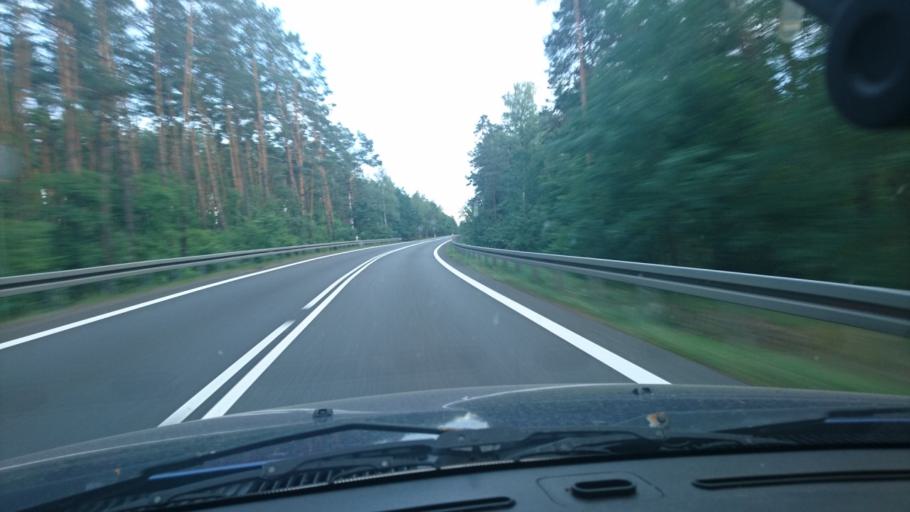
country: PL
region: Silesian Voivodeship
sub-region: Powiat lubliniecki
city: Lubliniec
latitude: 50.6024
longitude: 18.7007
